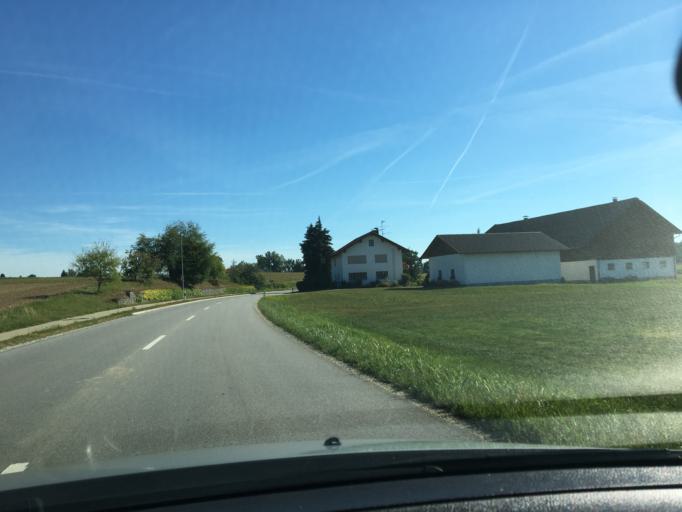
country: DE
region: Bavaria
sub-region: Lower Bavaria
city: Bodenkirchen
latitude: 48.3777
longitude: 12.3737
